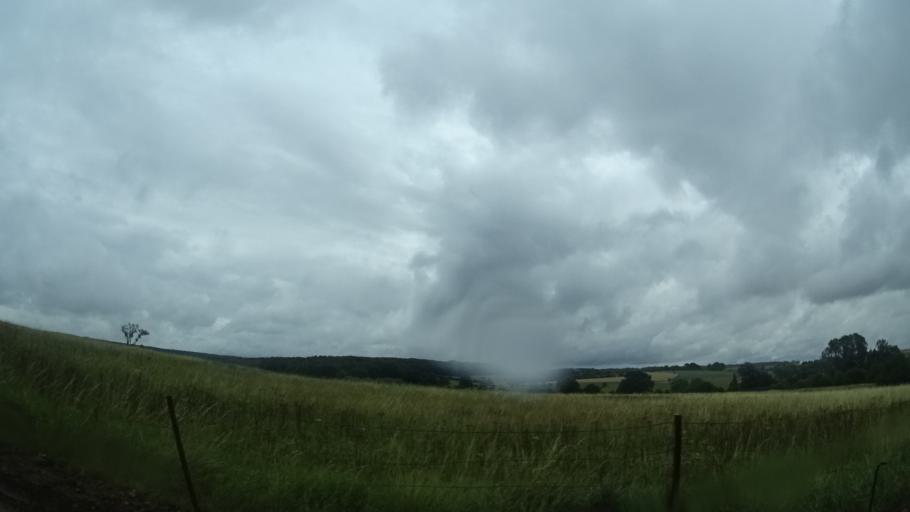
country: LU
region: Luxembourg
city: Bergem
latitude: 49.5202
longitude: 6.0514
